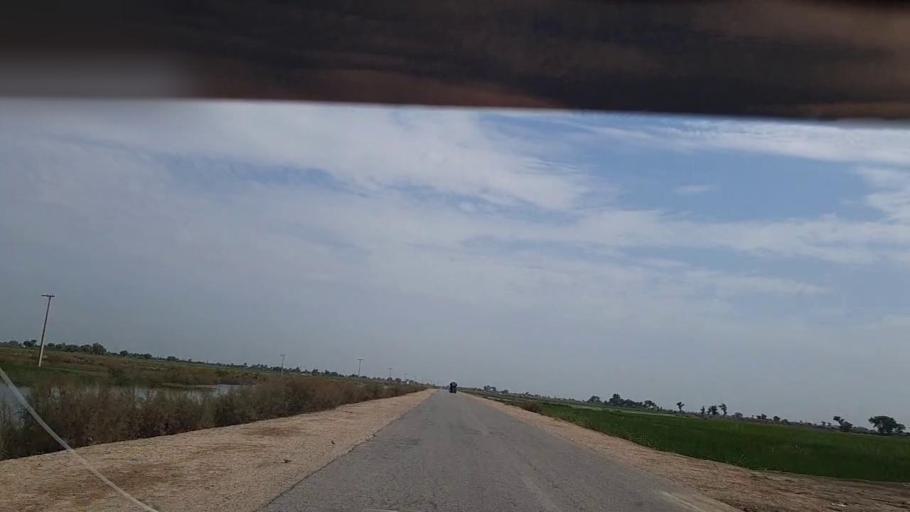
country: PK
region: Sindh
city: Thul
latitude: 28.1985
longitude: 68.7909
